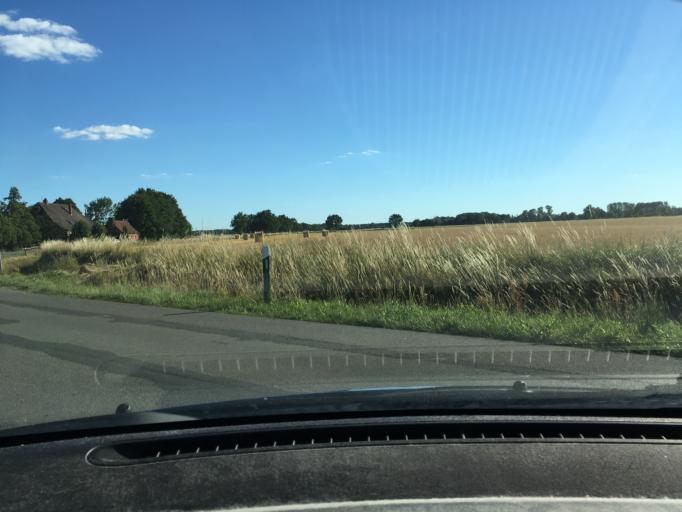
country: DE
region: Mecklenburg-Vorpommern
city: Boizenburg
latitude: 53.3456
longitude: 10.7240
